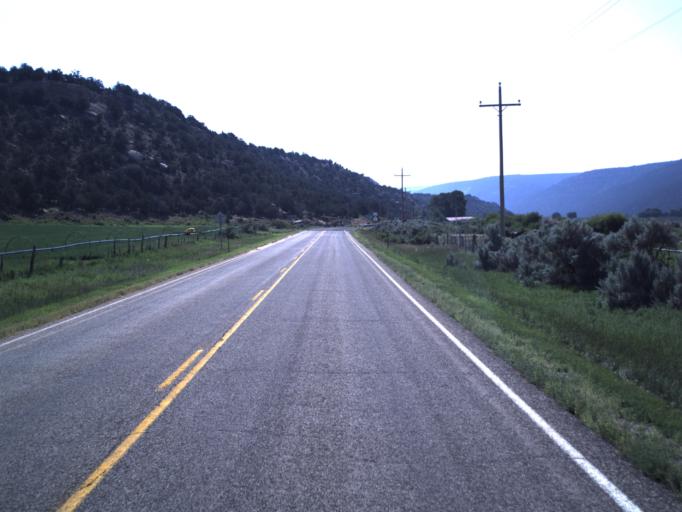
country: US
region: Utah
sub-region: Duchesne County
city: Duchesne
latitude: 40.3330
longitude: -110.6746
